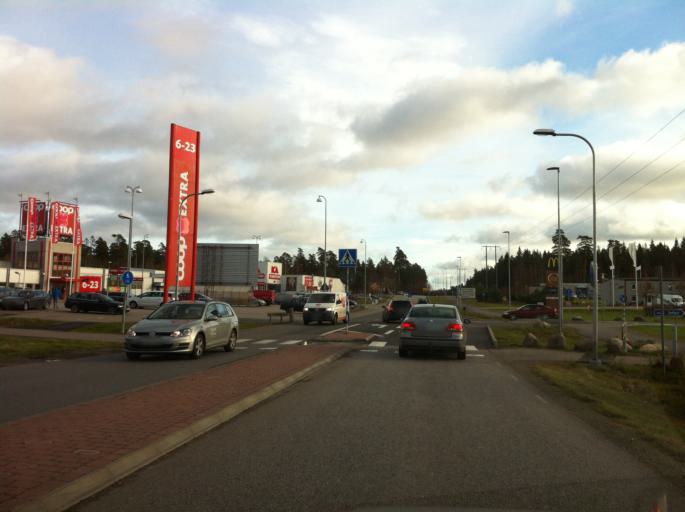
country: SE
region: Kronoberg
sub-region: Vaxjo Kommun
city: Vaexjoe
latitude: 56.8532
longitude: 14.7276
